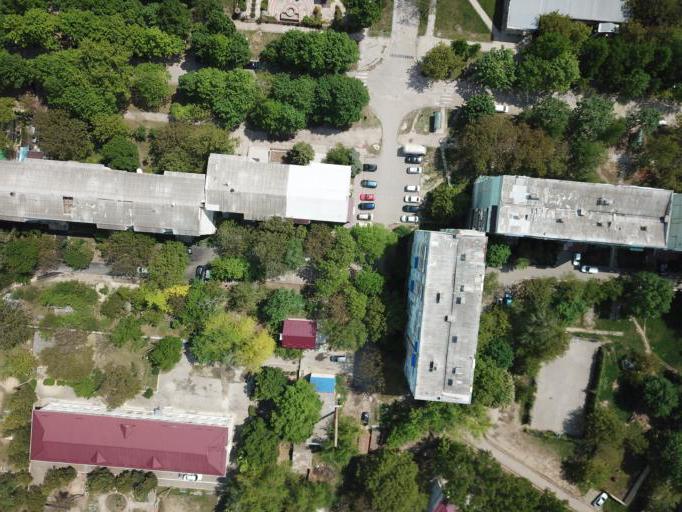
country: MD
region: Ungheni
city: Ungheni
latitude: 47.2152
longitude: 27.7983
